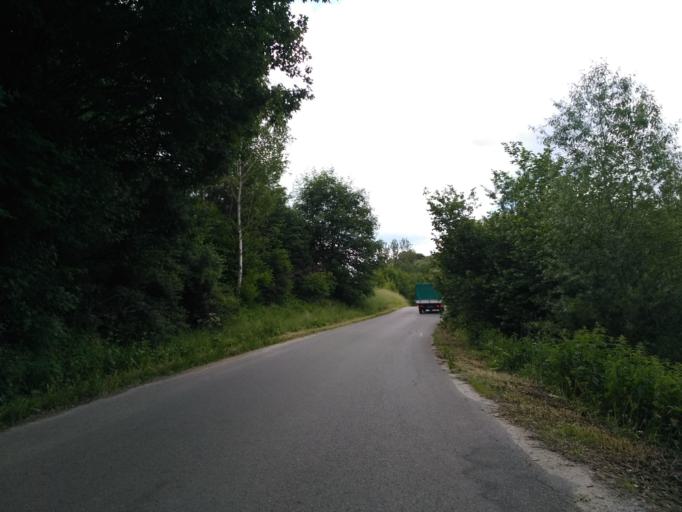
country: PL
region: Subcarpathian Voivodeship
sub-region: Powiat przeworski
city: Jawornik Polski
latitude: 49.8458
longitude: 22.3024
